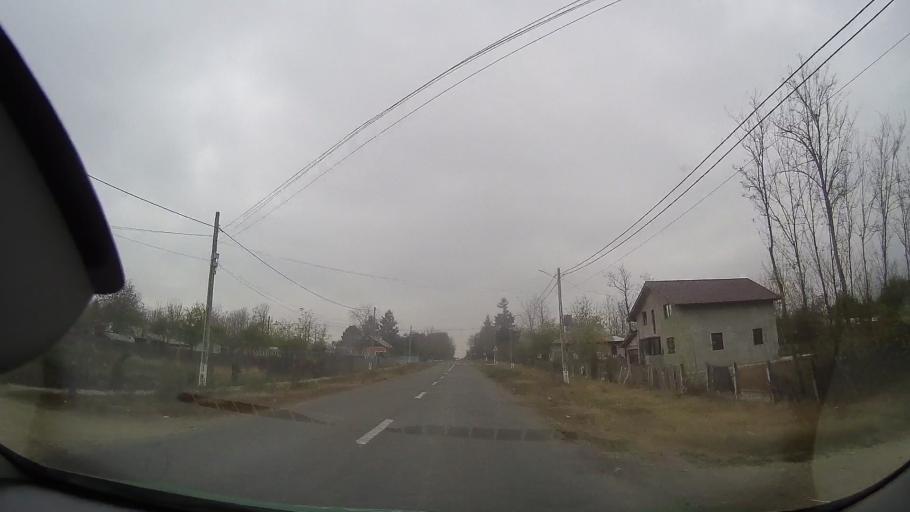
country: RO
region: Ialomita
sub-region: Comuna Valea Macrisului
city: Valea Macrisului
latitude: 44.7412
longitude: 26.8364
